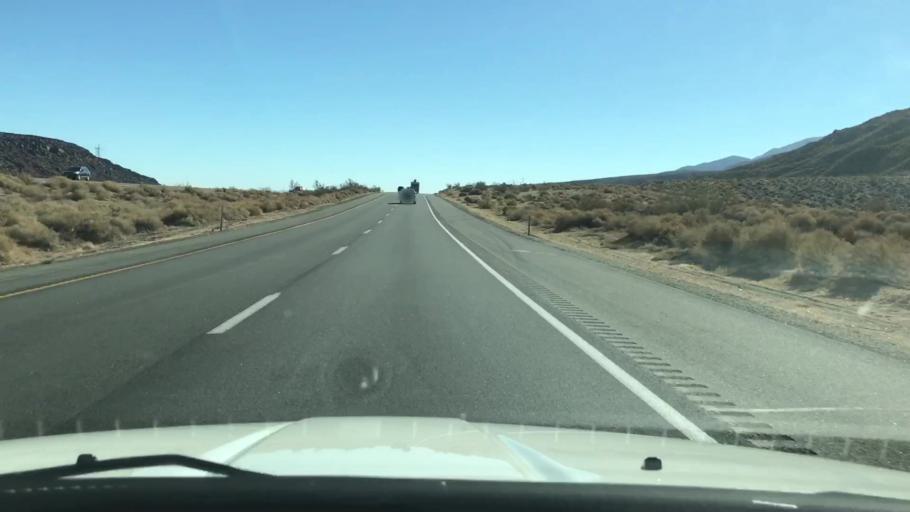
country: US
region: California
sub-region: Kern County
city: Inyokern
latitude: 35.9108
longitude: -117.9036
